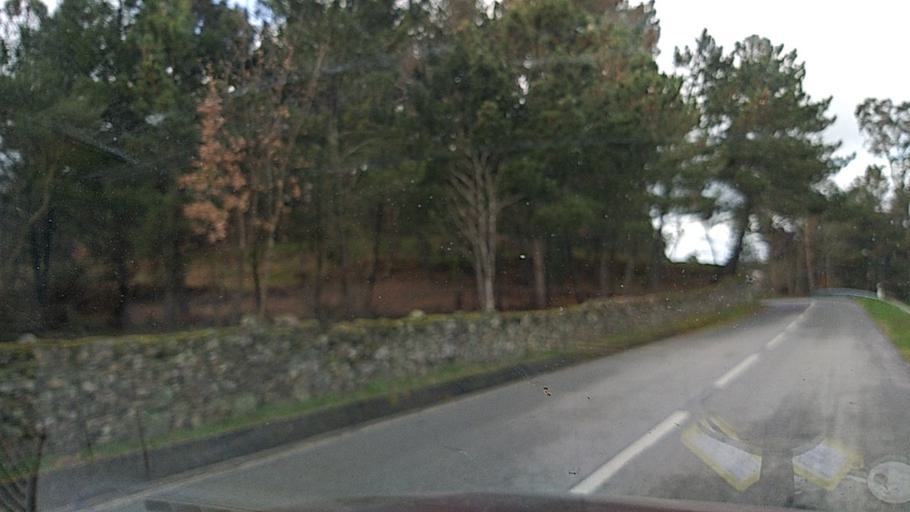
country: PT
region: Guarda
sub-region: Fornos de Algodres
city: Fornos de Algodres
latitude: 40.6567
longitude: -7.5553
